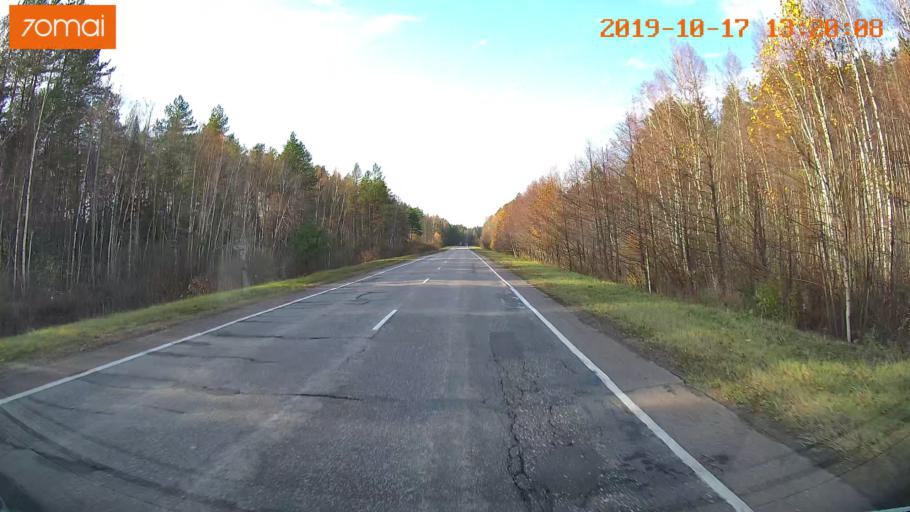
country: RU
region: Rjazan
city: Gus'-Zheleznyy
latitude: 55.0739
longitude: 41.0572
